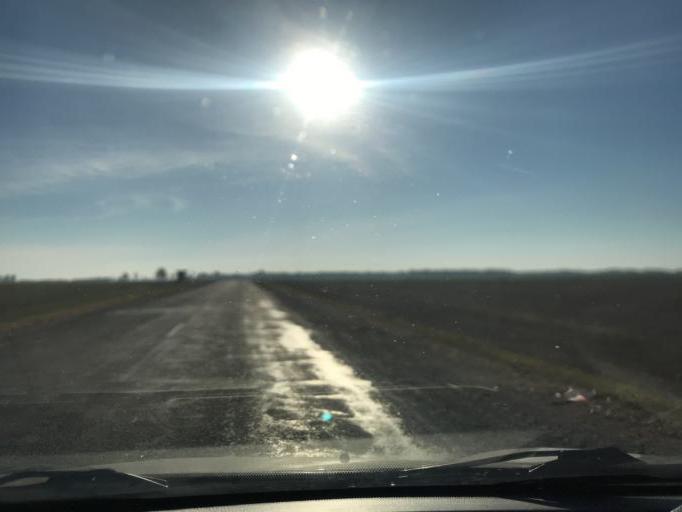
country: BY
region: Gomel
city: Brahin
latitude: 51.8071
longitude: 30.1125
